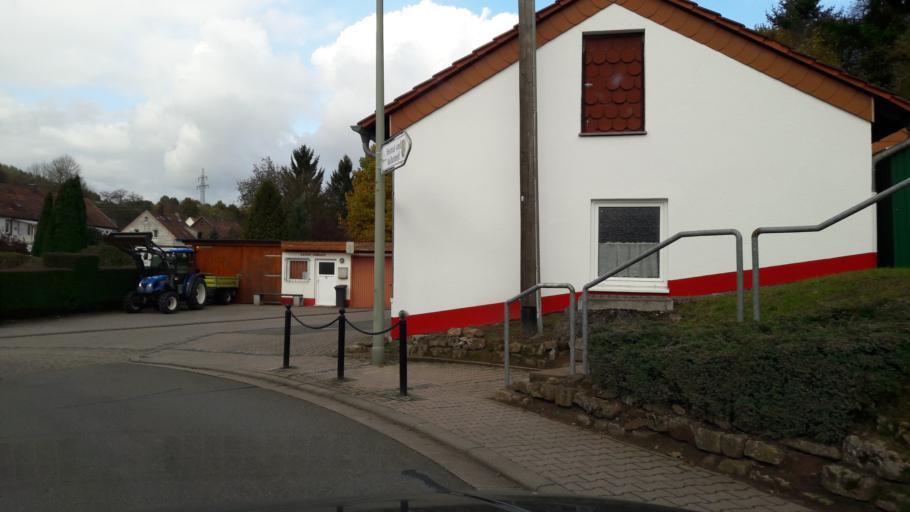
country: DE
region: Rheinland-Pfalz
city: Ohmbach
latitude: 49.4521
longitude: 7.3504
